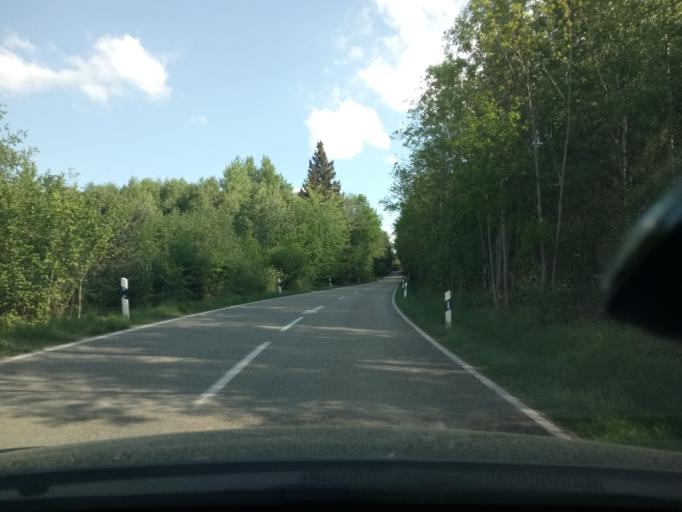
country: DE
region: Bavaria
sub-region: Upper Bavaria
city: Reichertsheim
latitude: 48.2117
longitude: 12.3011
